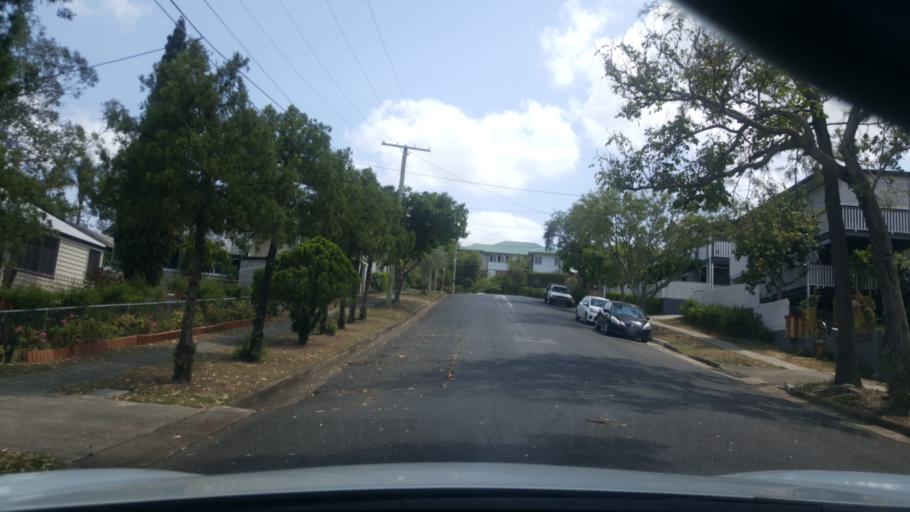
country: AU
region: Queensland
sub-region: Brisbane
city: South Brisbane
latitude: -27.4891
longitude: 153.0230
